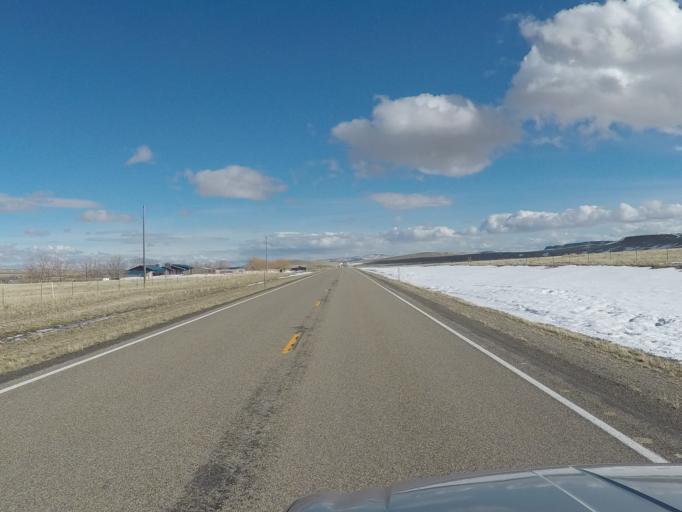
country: US
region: Montana
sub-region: Meagher County
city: White Sulphur Springs
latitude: 46.5288
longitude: -110.4217
